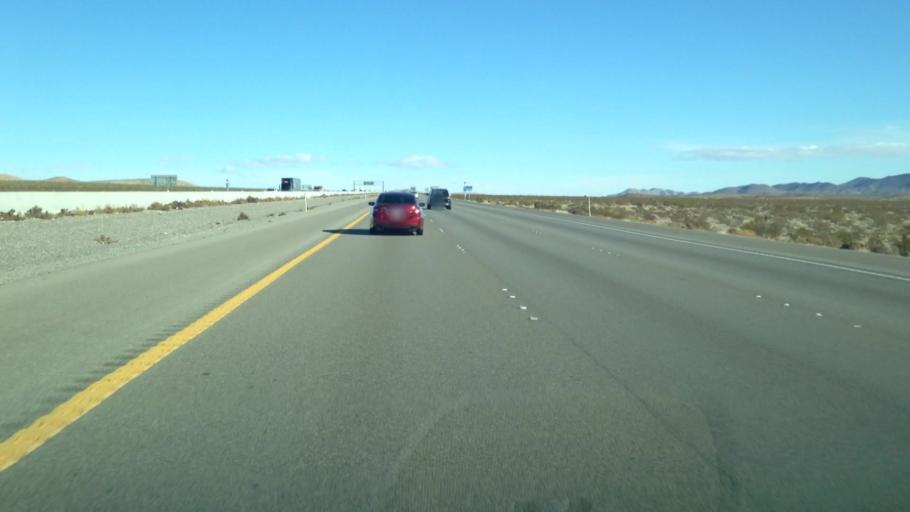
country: US
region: Nevada
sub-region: Clark County
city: Enterprise
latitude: 35.7961
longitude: -115.3168
